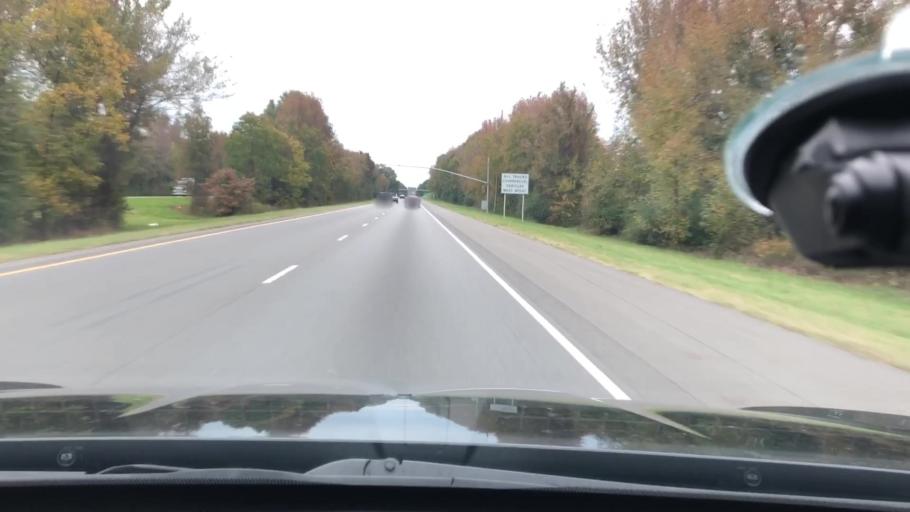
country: US
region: Arkansas
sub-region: Hempstead County
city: Hope
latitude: 33.6443
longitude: -93.6871
